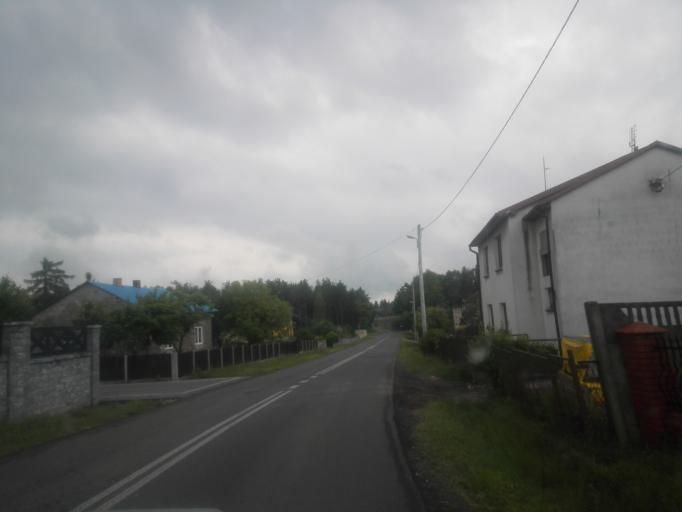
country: PL
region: Silesian Voivodeship
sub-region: Powiat czestochowski
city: Olsztyn
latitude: 50.7118
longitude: 19.3387
